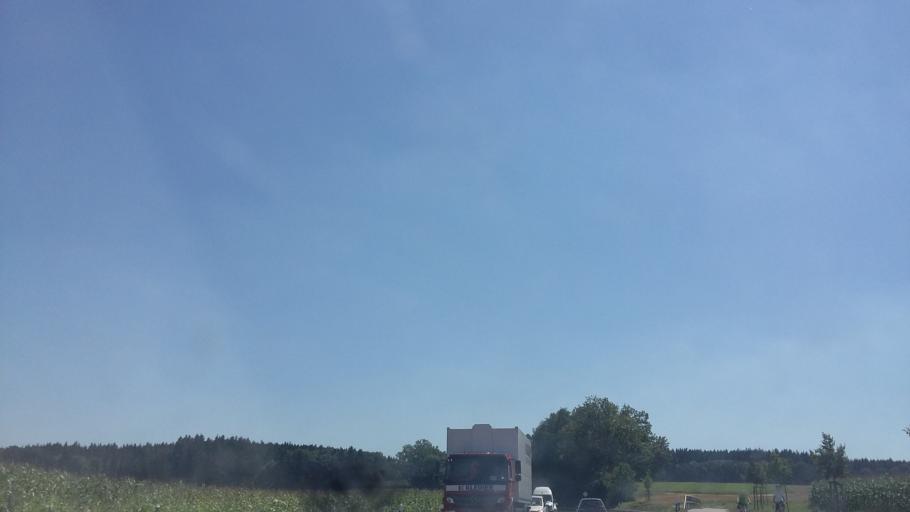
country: DE
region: Bavaria
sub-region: Upper Bavaria
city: Emmering
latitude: 48.1631
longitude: 11.2816
